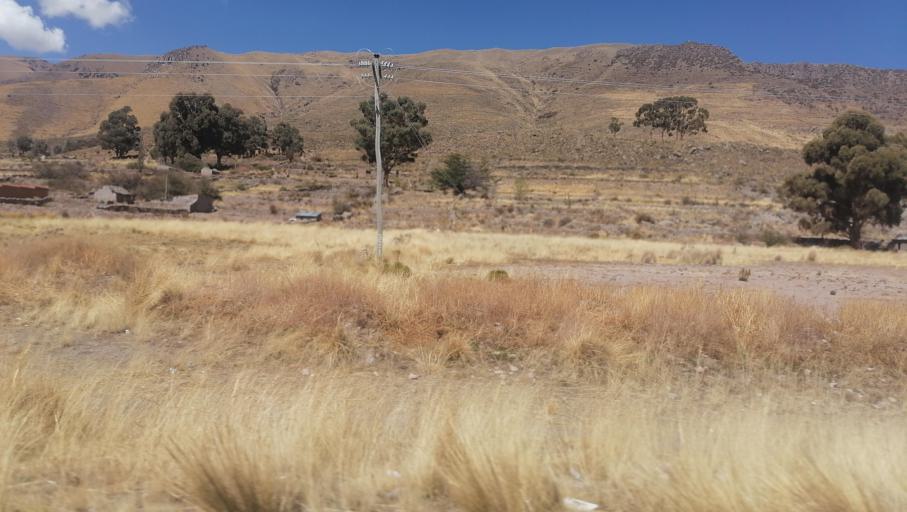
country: BO
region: Oruro
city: Challapata
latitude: -18.9932
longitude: -66.7782
